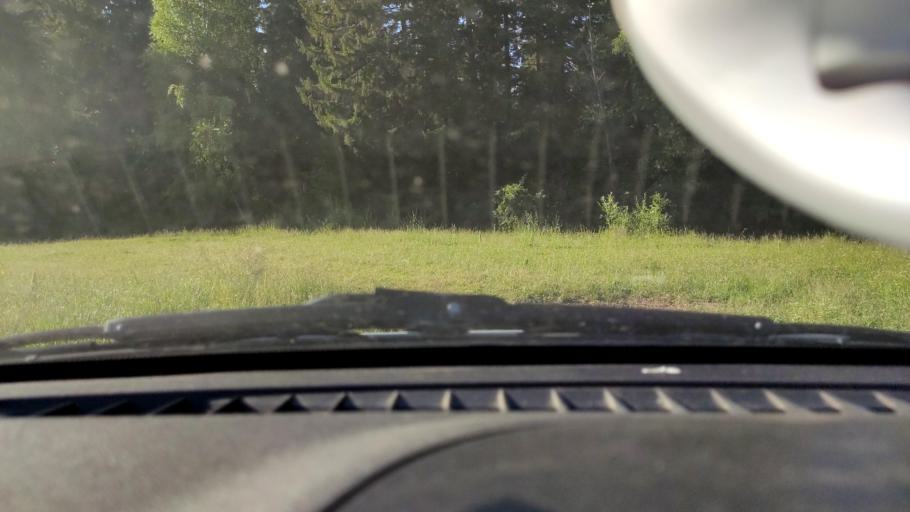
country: RU
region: Perm
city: Bershet'
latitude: 57.6971
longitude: 56.4186
